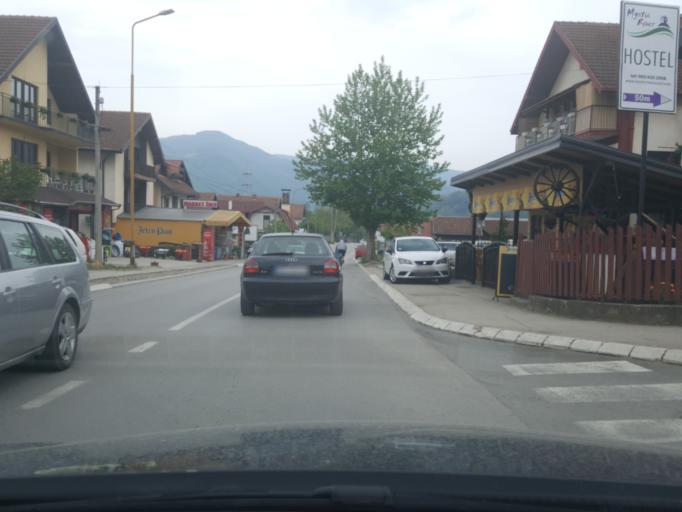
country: RS
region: Central Serbia
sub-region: Zlatiborski Okrug
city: Bajina Basta
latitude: 43.9775
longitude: 19.5690
